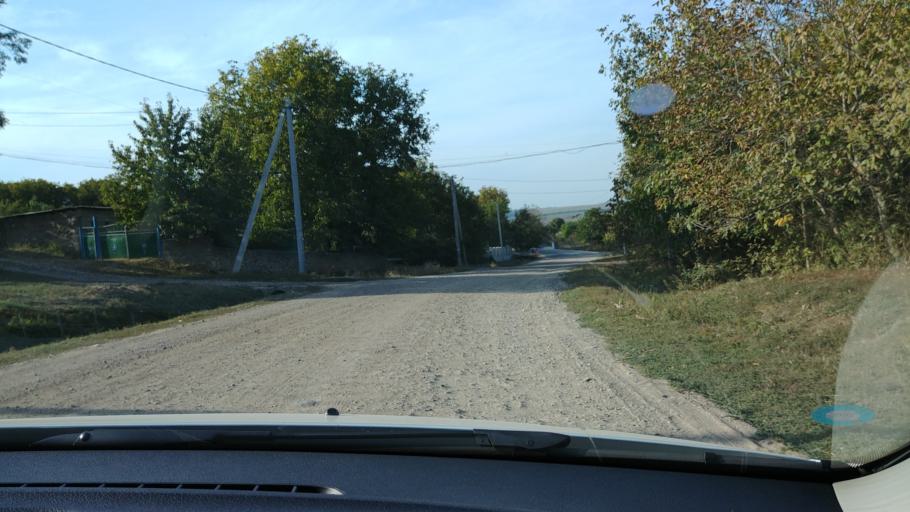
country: MD
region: Rezina
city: Rezina
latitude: 47.7477
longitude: 28.8850
